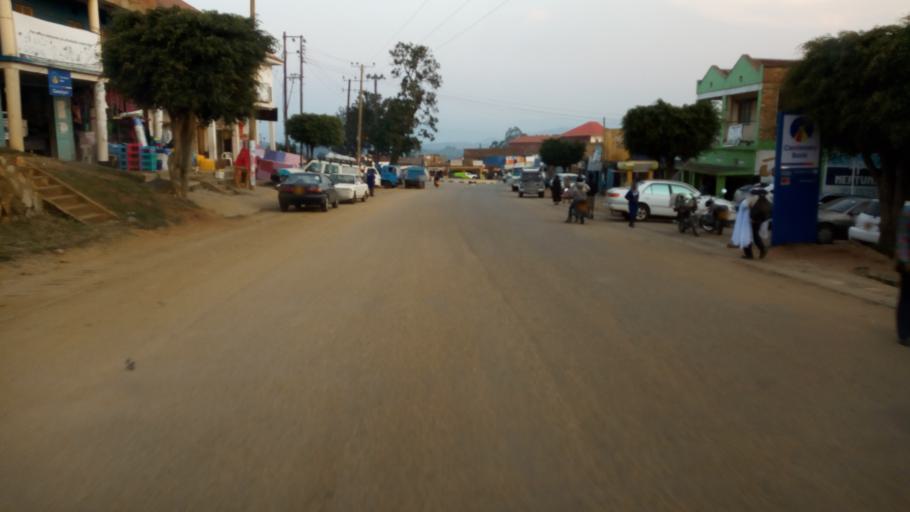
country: UG
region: Western Region
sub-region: Rukungiri District
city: Rukungiri
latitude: -0.7898
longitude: 29.9265
